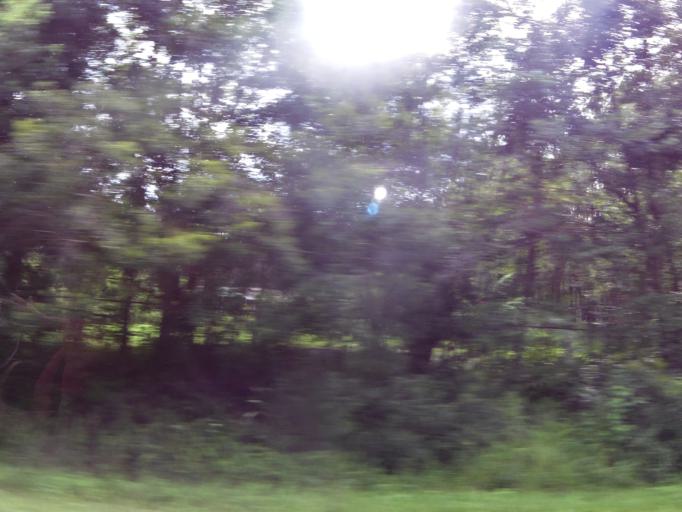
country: US
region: Florida
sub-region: Clay County
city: Asbury Lake
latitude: 30.0633
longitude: -81.7580
